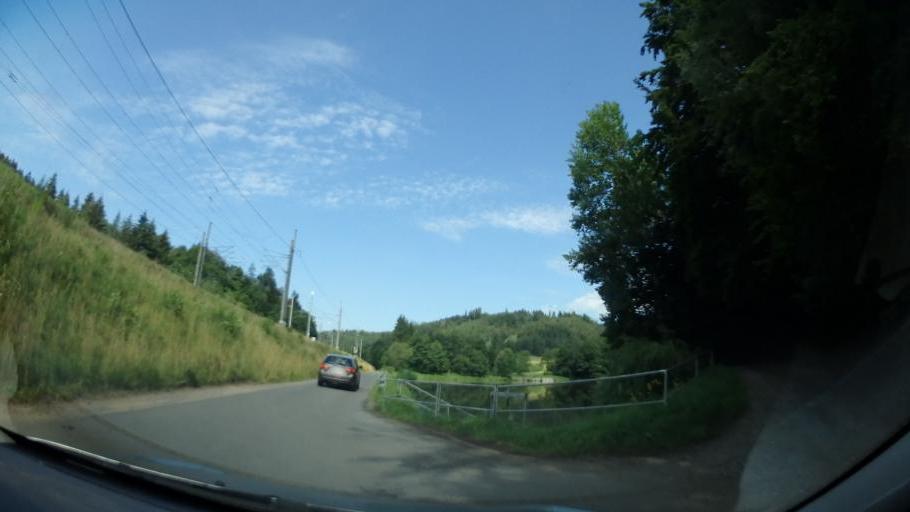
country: CZ
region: Olomoucky
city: Zabreh
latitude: 49.8646
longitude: 16.8096
